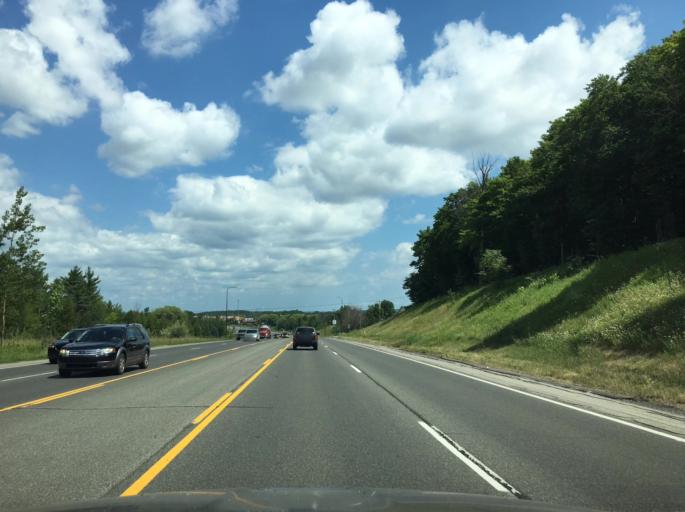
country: US
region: Michigan
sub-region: Grand Traverse County
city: Traverse City
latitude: 44.7144
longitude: -85.6482
